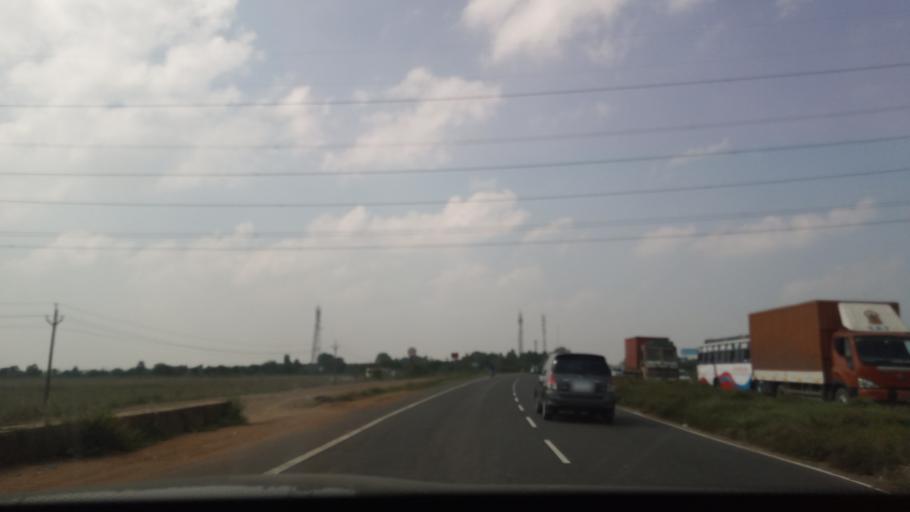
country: IN
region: Tamil Nadu
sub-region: Kancheepuram
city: Kanchipuram
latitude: 12.8779
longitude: 79.7762
